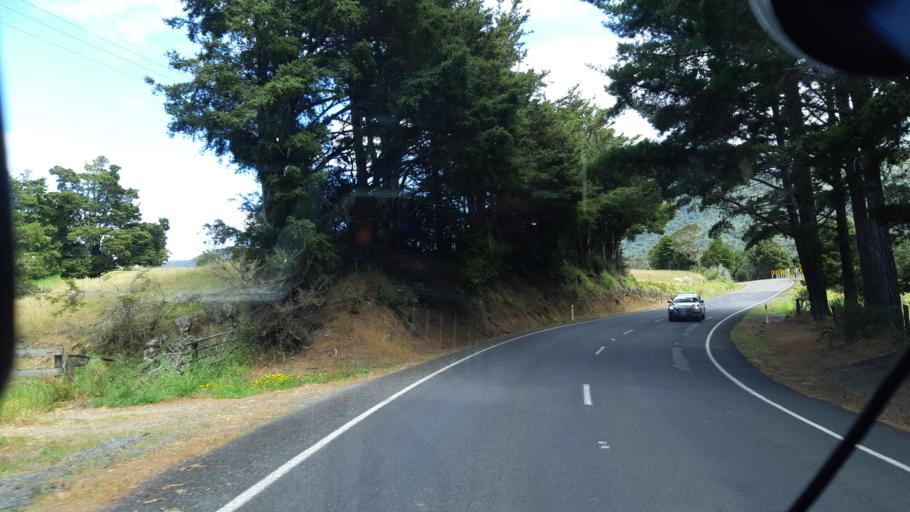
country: NZ
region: Northland
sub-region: Far North District
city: Waimate North
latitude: -35.2914
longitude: 173.7252
